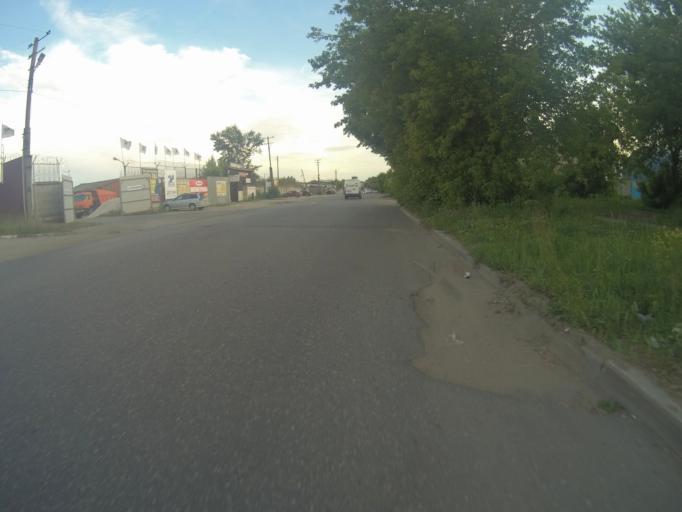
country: RU
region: Vladimir
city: Vladimir
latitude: 56.1570
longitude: 40.3838
